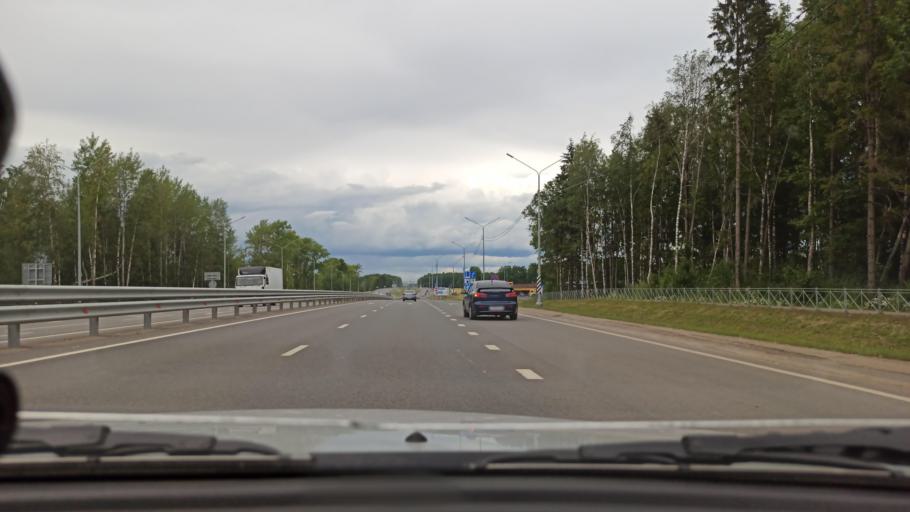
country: RU
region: Vologda
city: Molochnoye
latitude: 59.2604
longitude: 39.7492
